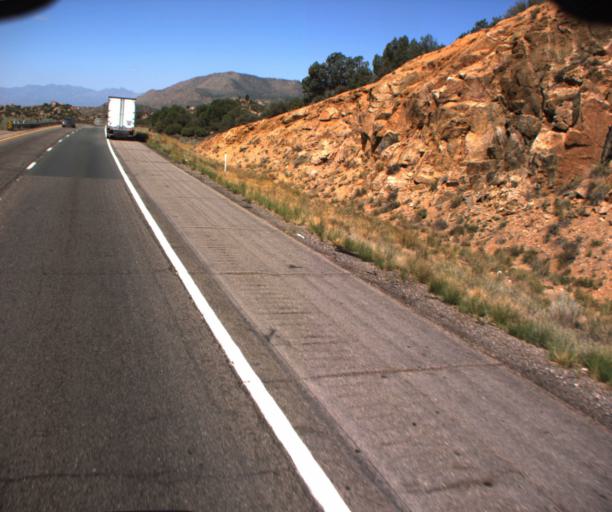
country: US
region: Arizona
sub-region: Mohave County
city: Peach Springs
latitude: 35.1801
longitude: -113.4783
